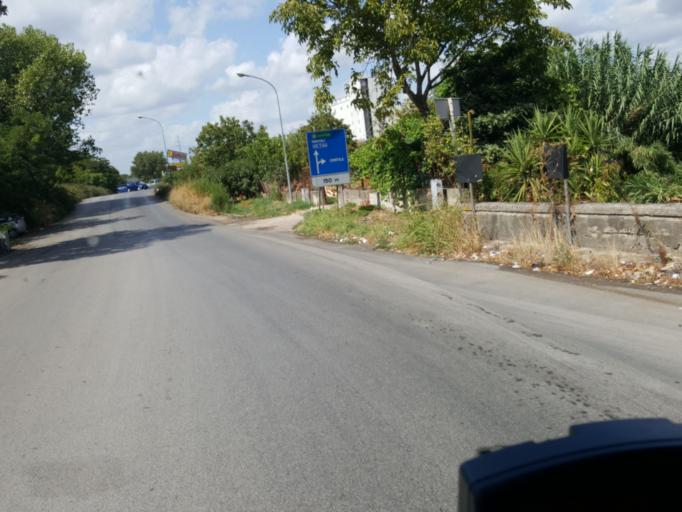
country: IT
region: Campania
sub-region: Provincia di Napoli
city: Cimitile
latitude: 40.9334
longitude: 14.5077
